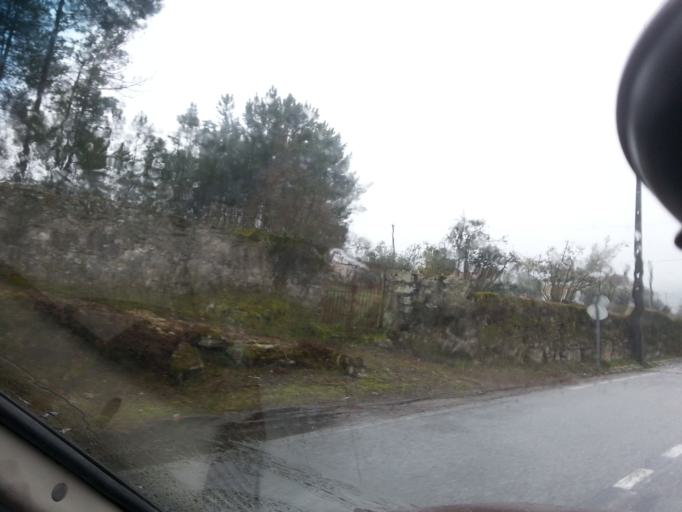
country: PT
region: Guarda
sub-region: Fornos de Algodres
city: Fornos de Algodres
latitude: 40.6086
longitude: -7.6415
